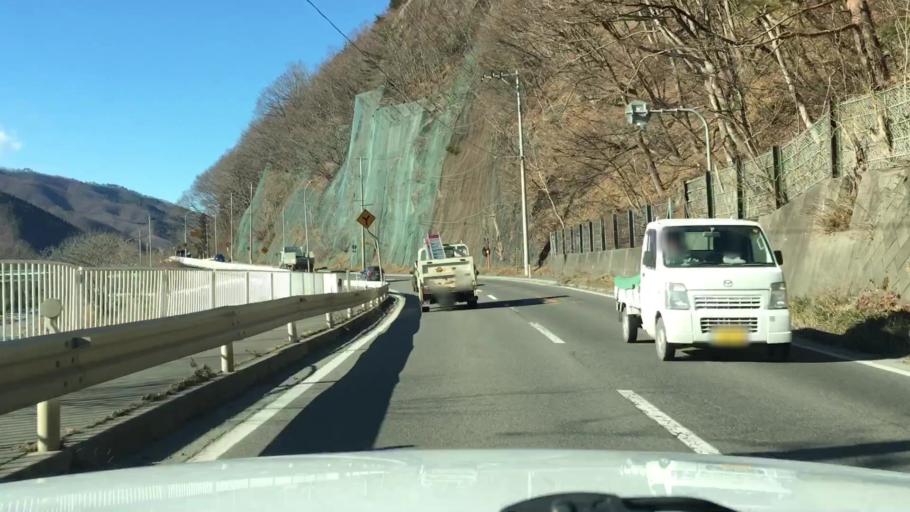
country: JP
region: Iwate
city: Miyako
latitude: 39.6198
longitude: 141.8059
